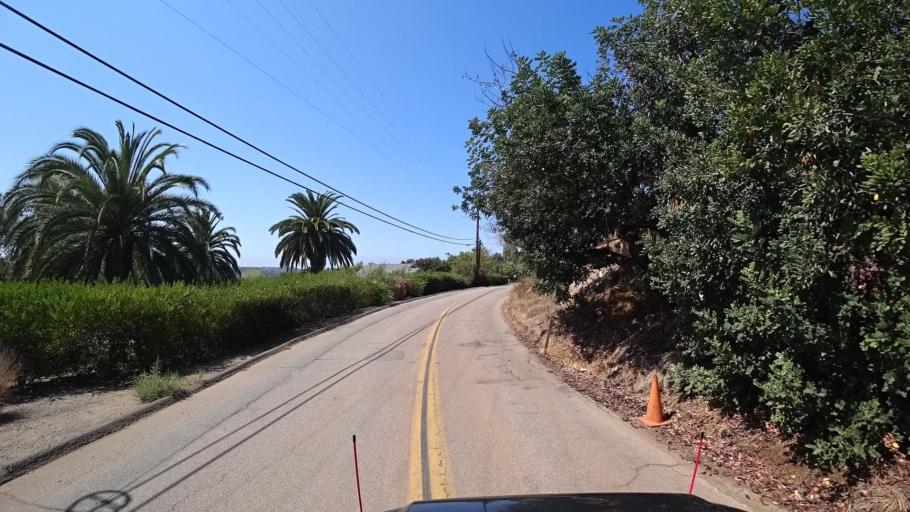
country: US
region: California
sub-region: San Diego County
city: Lake San Marcos
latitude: 33.1668
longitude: -117.2008
